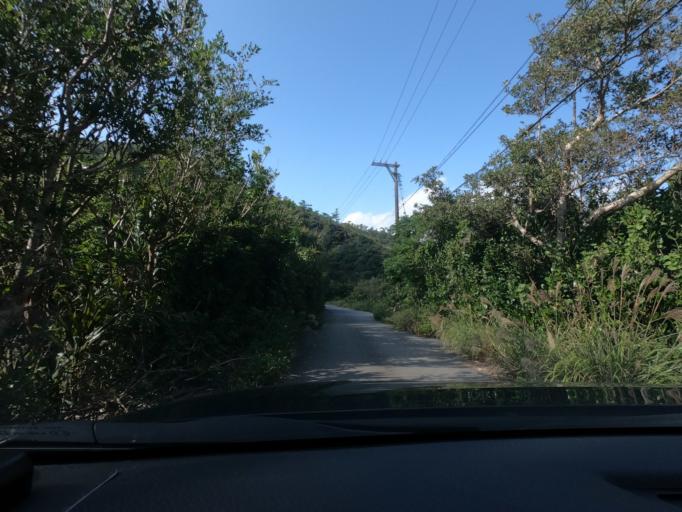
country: JP
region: Okinawa
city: Nago
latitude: 26.7645
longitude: 128.2149
